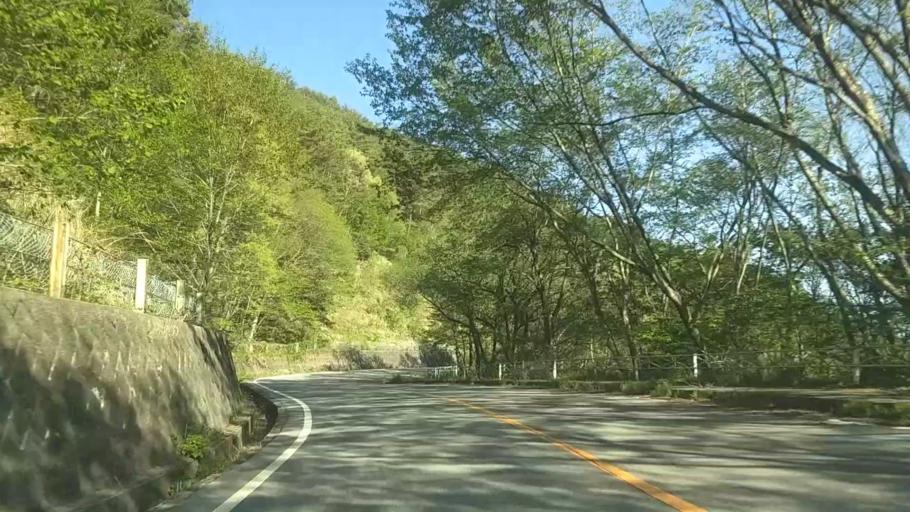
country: JP
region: Yamanashi
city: Nirasaki
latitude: 35.9071
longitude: 138.3801
